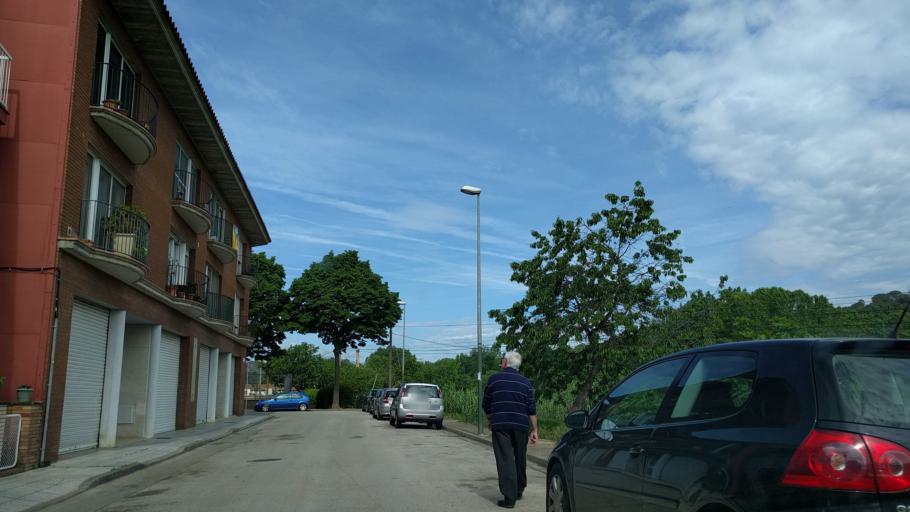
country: ES
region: Catalonia
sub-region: Provincia de Girona
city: Bescano
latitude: 41.9679
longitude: 2.7387
